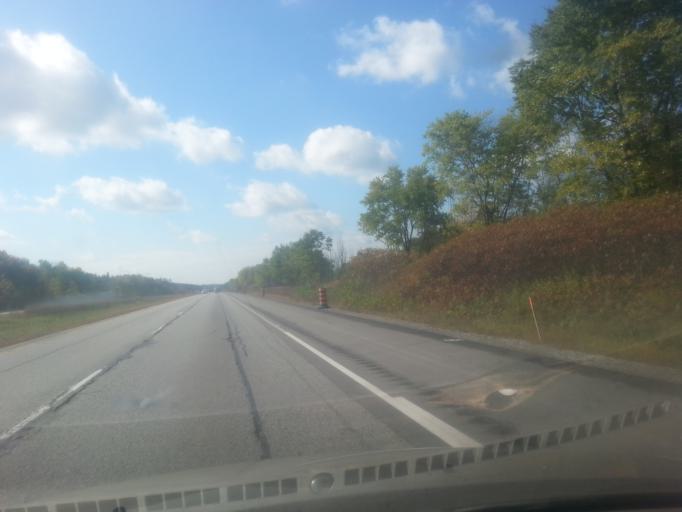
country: US
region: New York
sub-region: Jefferson County
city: Alexandria Bay
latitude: 44.4720
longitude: -75.8716
